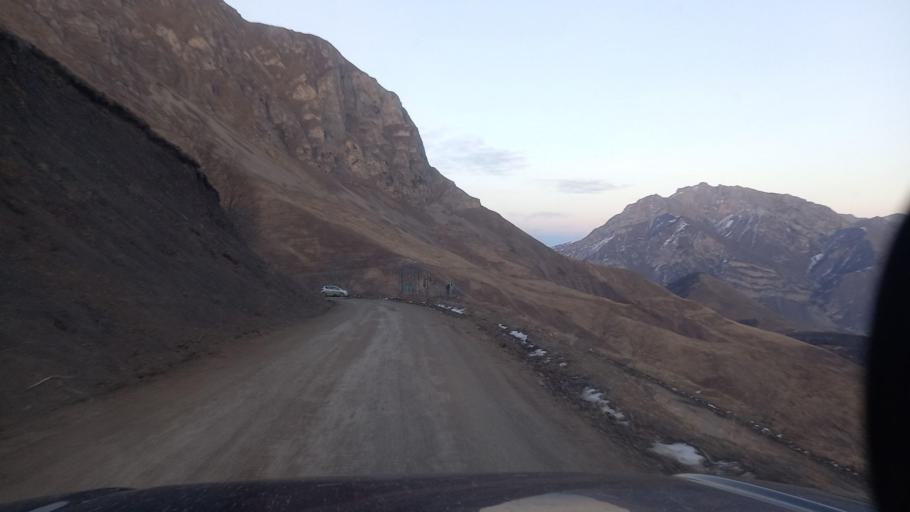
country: RU
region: Ingushetiya
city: Dzhayrakh
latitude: 42.8343
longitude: 44.5682
